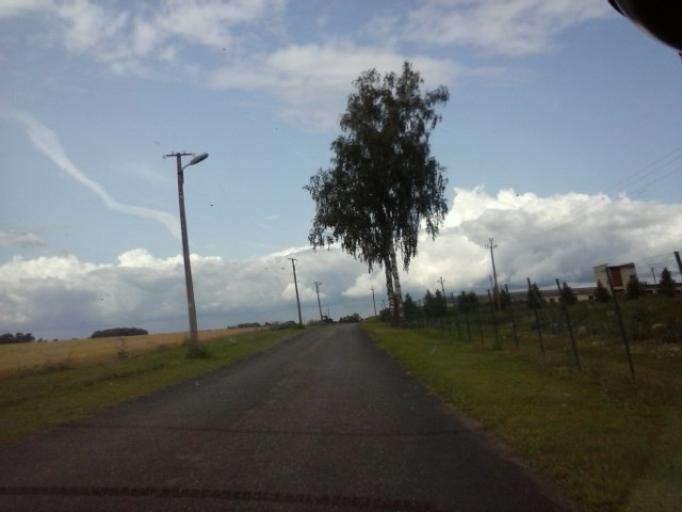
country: EE
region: Tartu
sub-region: Tartu linn
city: Tartu
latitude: 58.3626
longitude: 26.8754
